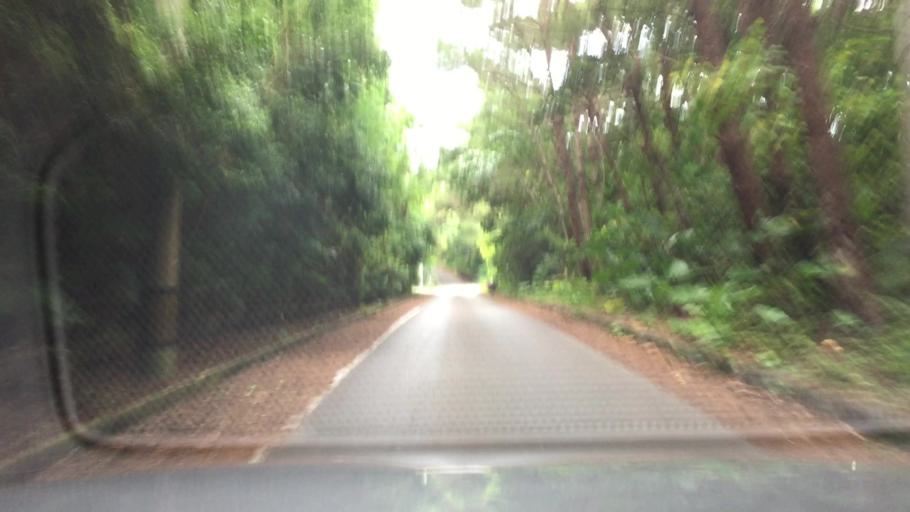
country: JP
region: Okinawa
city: Ishigaki
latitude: 24.4511
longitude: 124.1359
